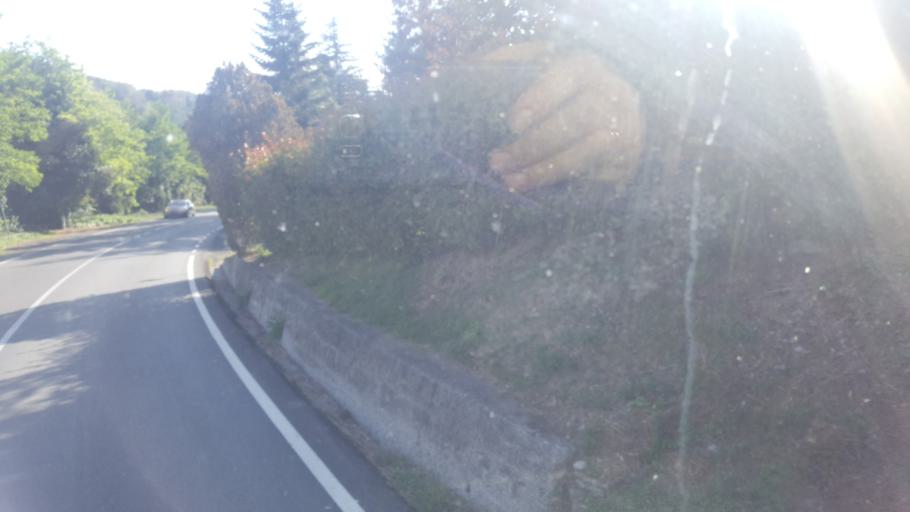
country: IT
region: Liguria
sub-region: Provincia di Genova
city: Savignone
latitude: 44.5843
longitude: 8.9837
